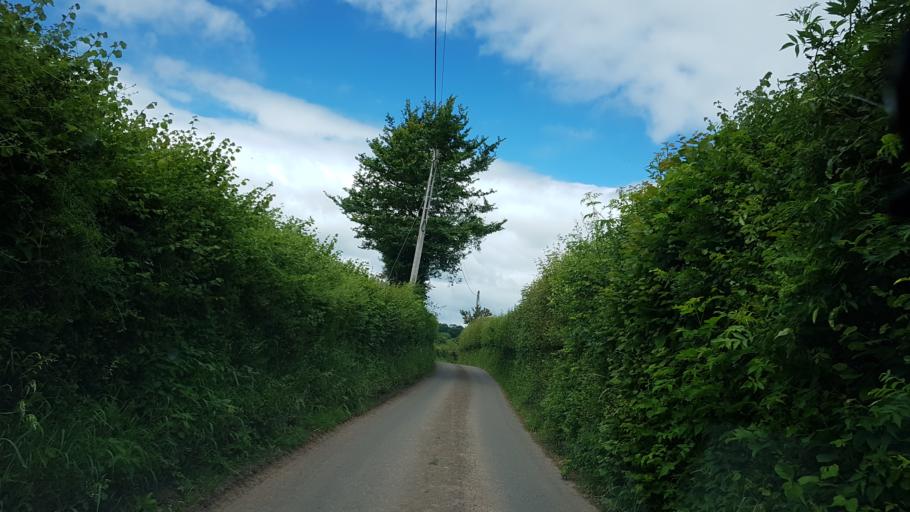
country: GB
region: Wales
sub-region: Monmouthshire
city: Llanarth
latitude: 51.8385
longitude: -2.8869
